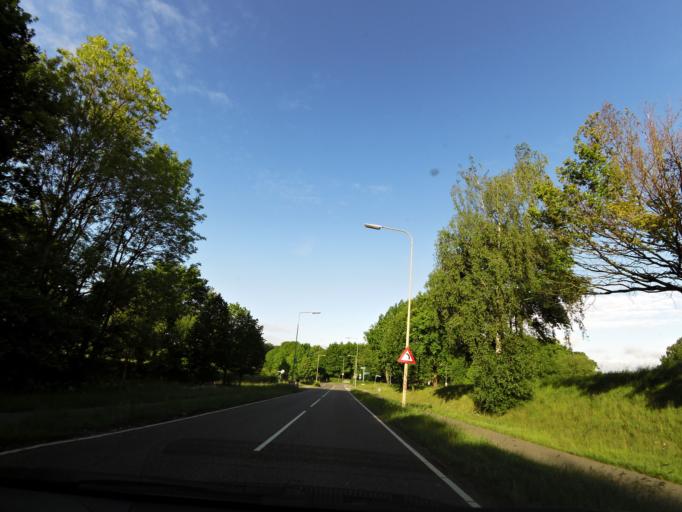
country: NL
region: Limburg
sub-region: Gemeente Voerendaal
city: Voerendaal
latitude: 50.8978
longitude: 5.9283
